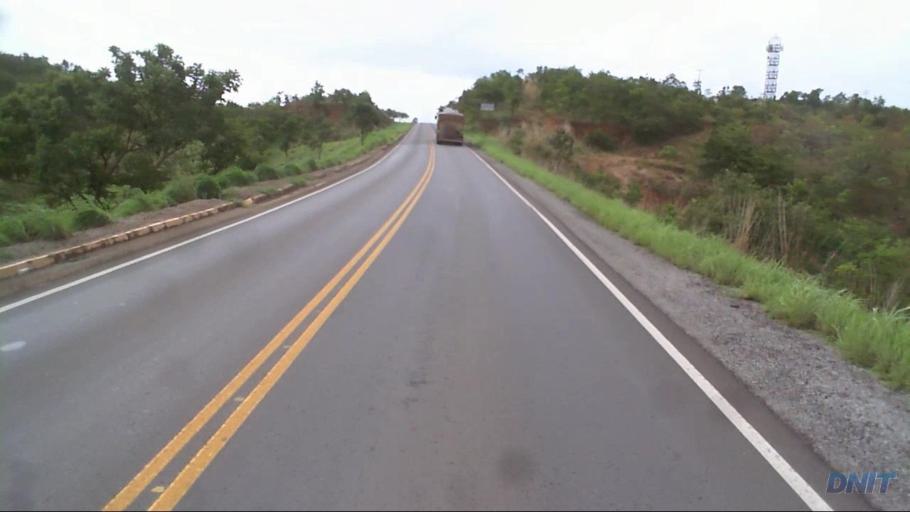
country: BR
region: Goias
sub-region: Padre Bernardo
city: Padre Bernardo
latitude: -15.2218
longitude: -48.2799
